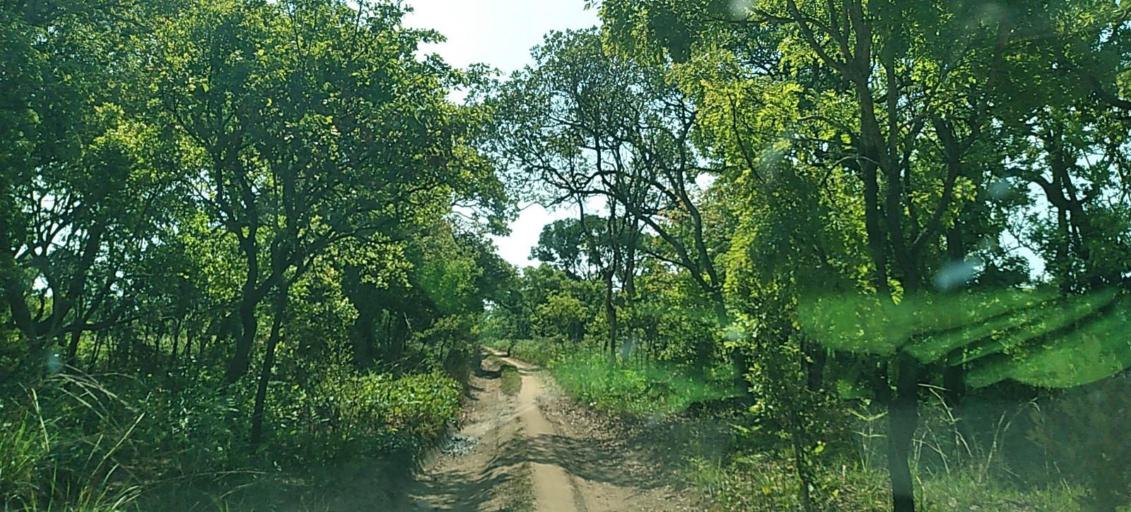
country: ZM
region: North-Western
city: Mwinilunga
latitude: -11.2728
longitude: 24.9819
